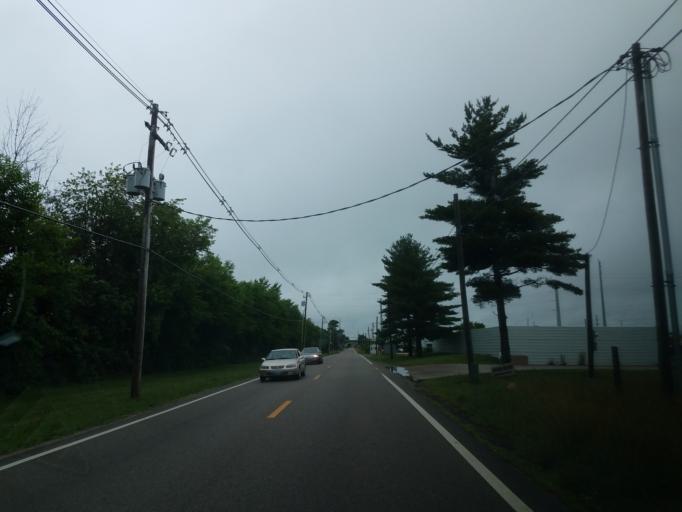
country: US
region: Illinois
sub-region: McLean County
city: Bloomington
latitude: 40.4544
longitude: -88.9814
